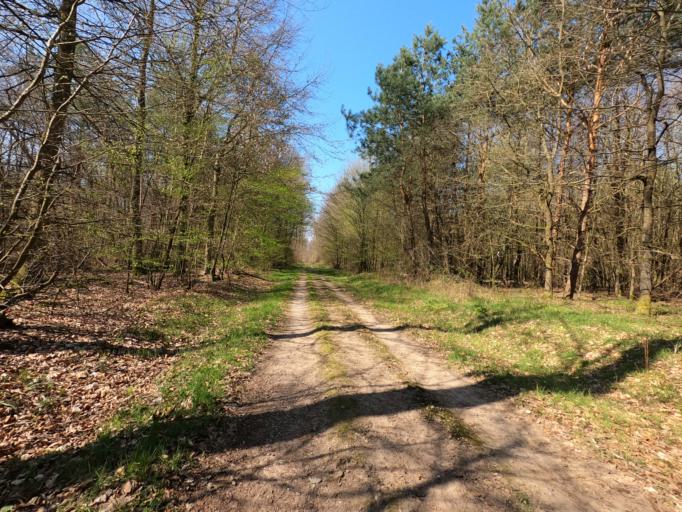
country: DE
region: Hesse
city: Morfelden-Walldorf
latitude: 49.9580
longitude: 8.5607
